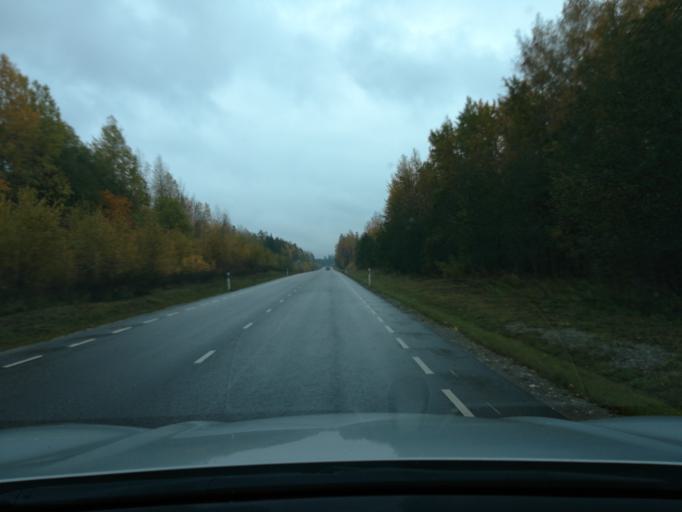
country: EE
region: Ida-Virumaa
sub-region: Johvi vald
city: Johvi
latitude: 59.3075
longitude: 27.4595
